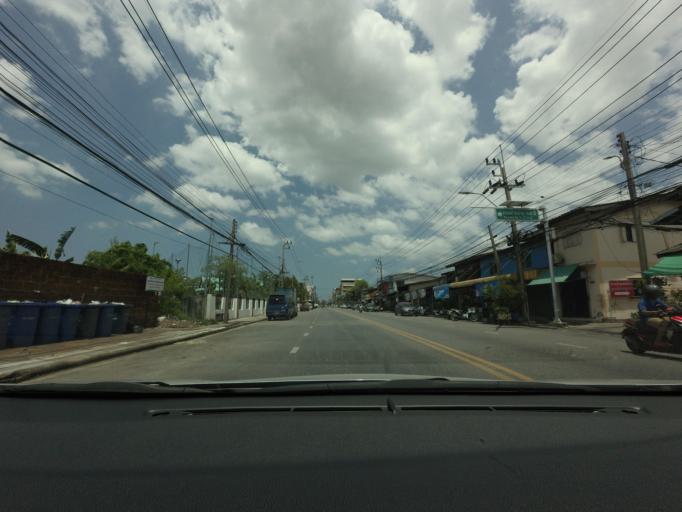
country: TH
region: Samut Prakan
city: Samut Prakan
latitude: 13.5889
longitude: 100.5961
